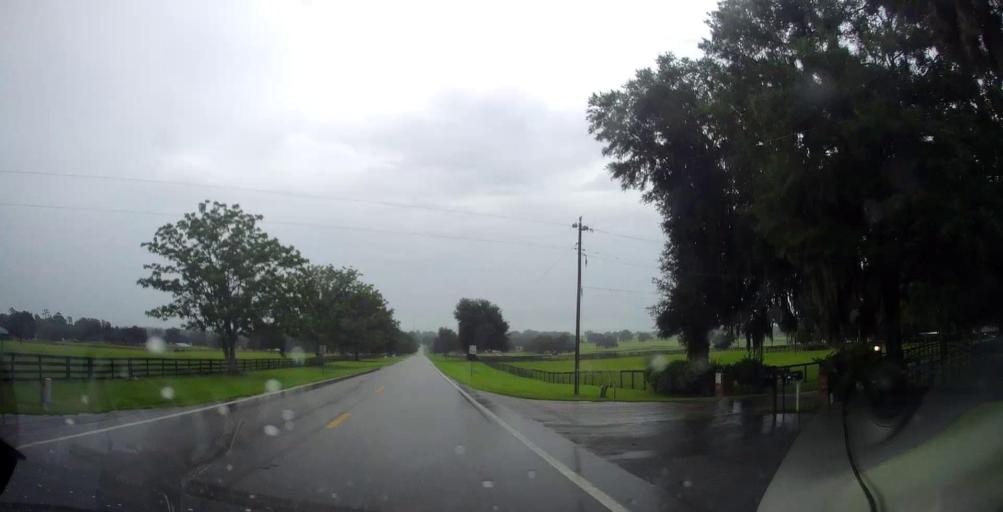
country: US
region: Florida
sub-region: Marion County
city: Citra
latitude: 29.3576
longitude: -82.2432
